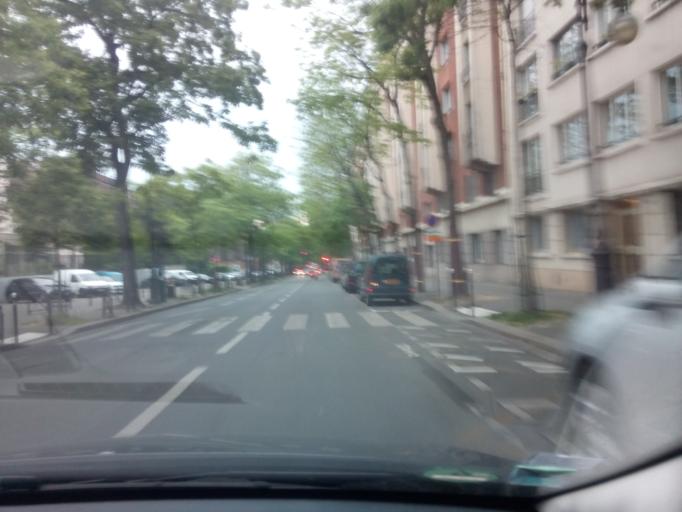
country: FR
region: Ile-de-France
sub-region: Departement du Val-de-Marne
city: Gentilly
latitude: 48.8272
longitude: 2.3365
